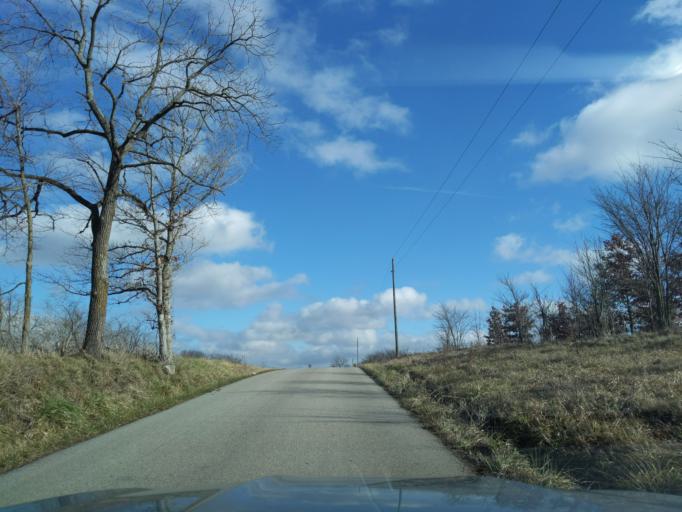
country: US
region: Indiana
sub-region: Decatur County
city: Greensburg
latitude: 39.2781
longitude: -85.4836
